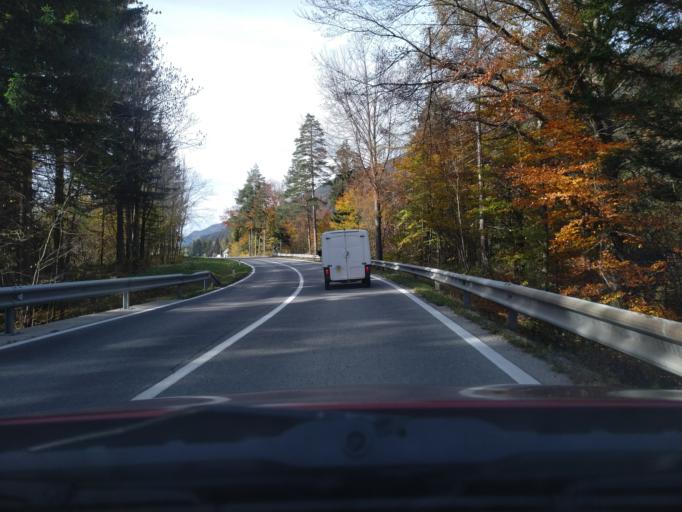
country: SI
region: Kranjska Gora
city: Kranjska Gora
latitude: 46.4868
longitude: 13.8162
